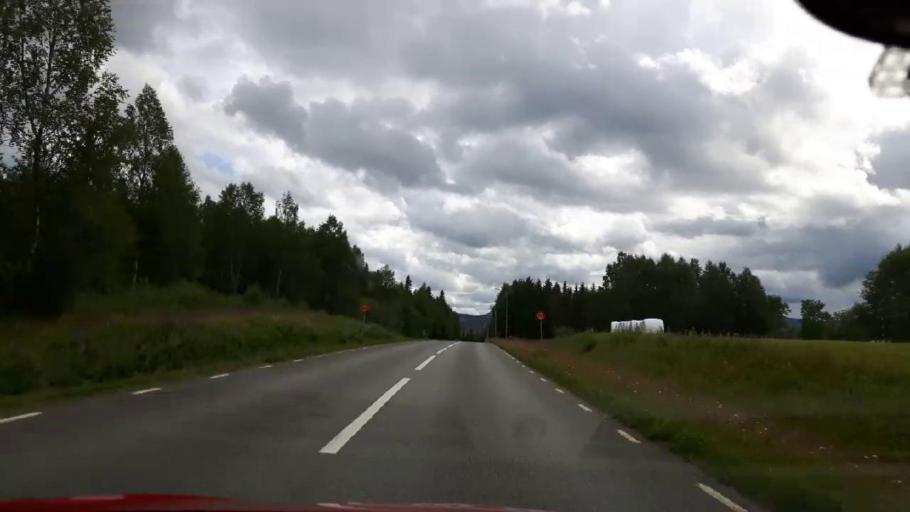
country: NO
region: Nord-Trondelag
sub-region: Lierne
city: Sandvika
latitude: 64.3939
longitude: 14.3674
